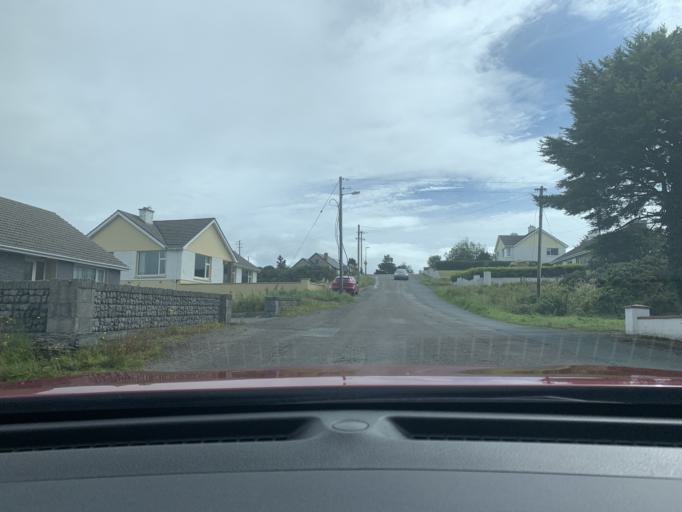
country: IE
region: Ulster
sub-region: County Donegal
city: Dungloe
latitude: 54.9448
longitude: -8.3584
